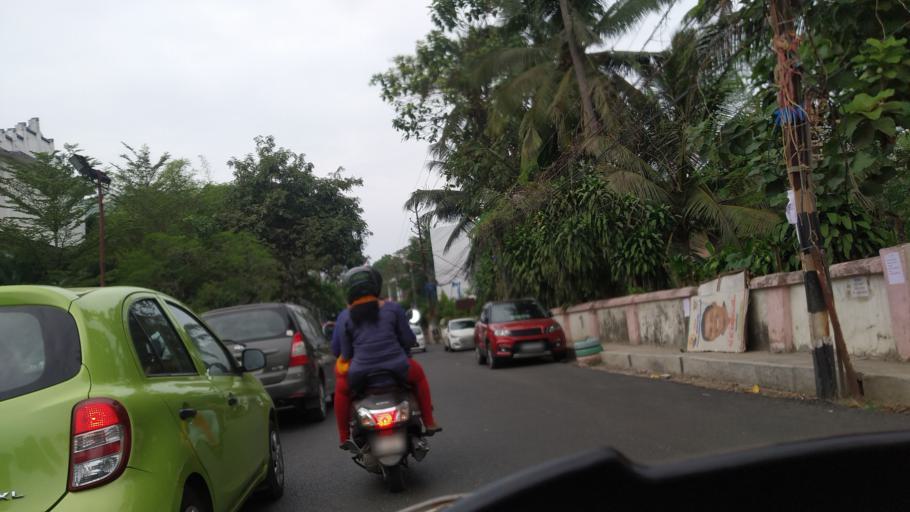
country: IN
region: Kerala
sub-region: Ernakulam
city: Cochin
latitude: 9.9392
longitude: 76.2964
